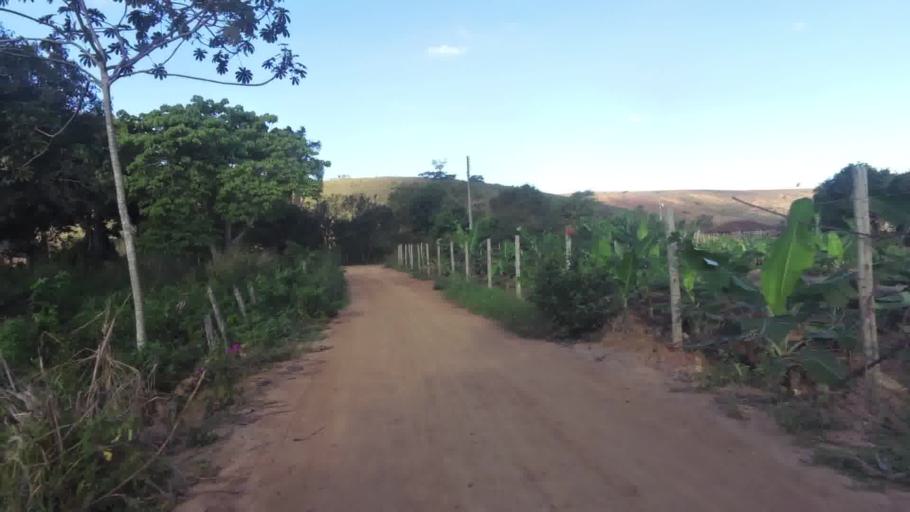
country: BR
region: Espirito Santo
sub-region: Marataizes
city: Marataizes
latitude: -21.1625
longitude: -41.0375
